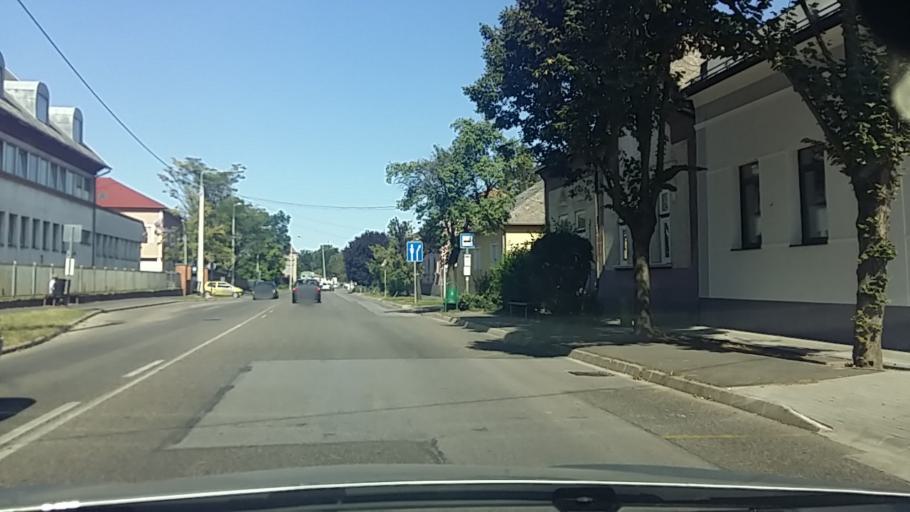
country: HU
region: Szabolcs-Szatmar-Bereg
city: Nyiregyhaza
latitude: 47.9508
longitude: 21.7332
